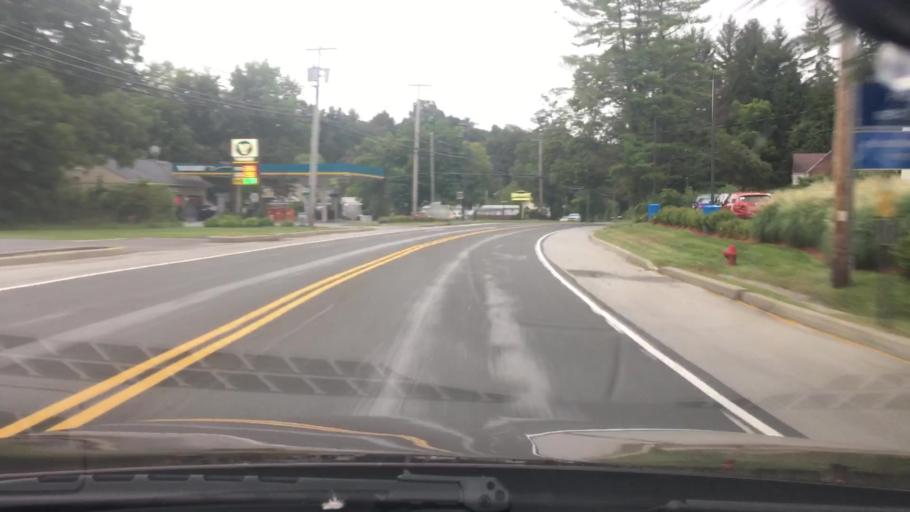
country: US
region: New York
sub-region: Dutchess County
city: Pleasant Valley
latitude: 41.7184
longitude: -73.8527
